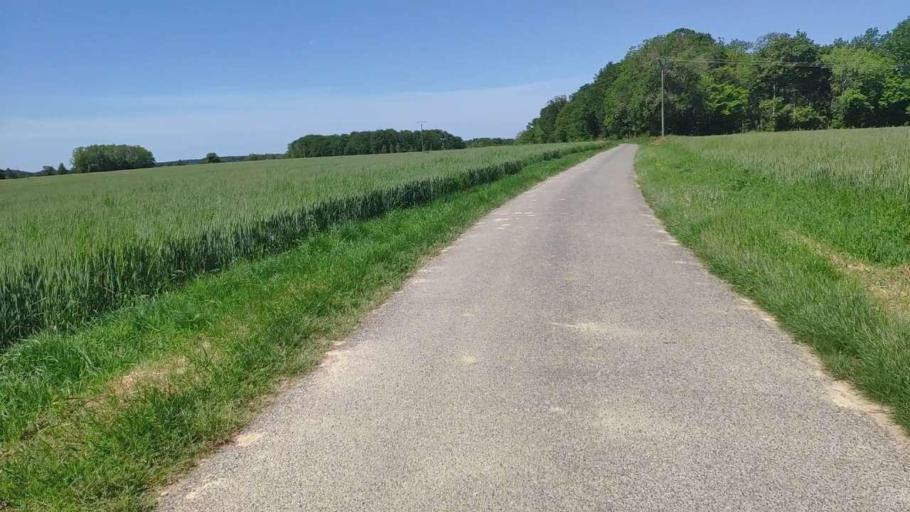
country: FR
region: Franche-Comte
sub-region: Departement du Jura
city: Bletterans
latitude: 46.7852
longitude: 5.4307
